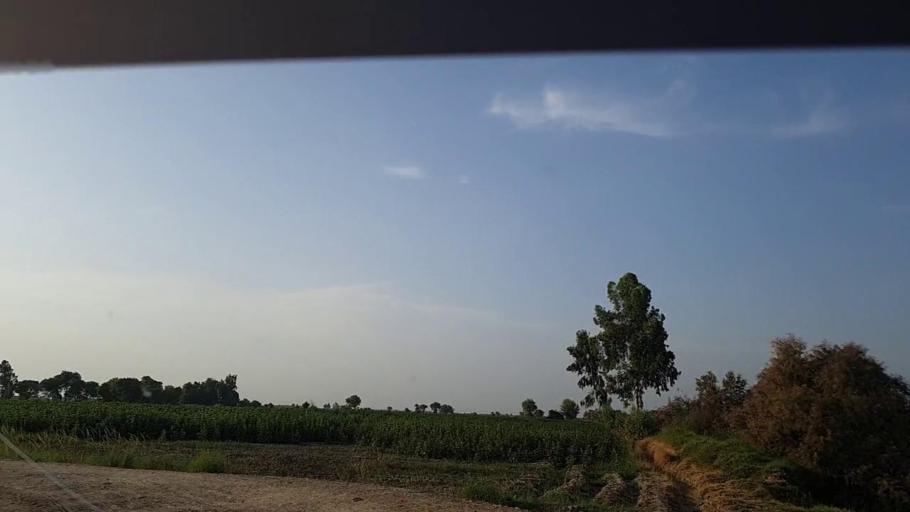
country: PK
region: Sindh
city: Khanpur
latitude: 27.8087
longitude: 69.3248
